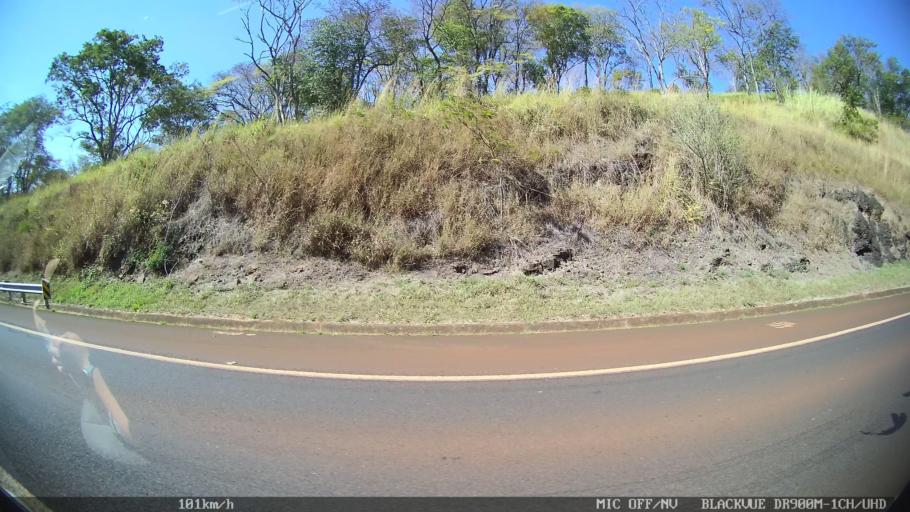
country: BR
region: Sao Paulo
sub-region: Franca
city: Franca
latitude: -20.6221
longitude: -47.4603
